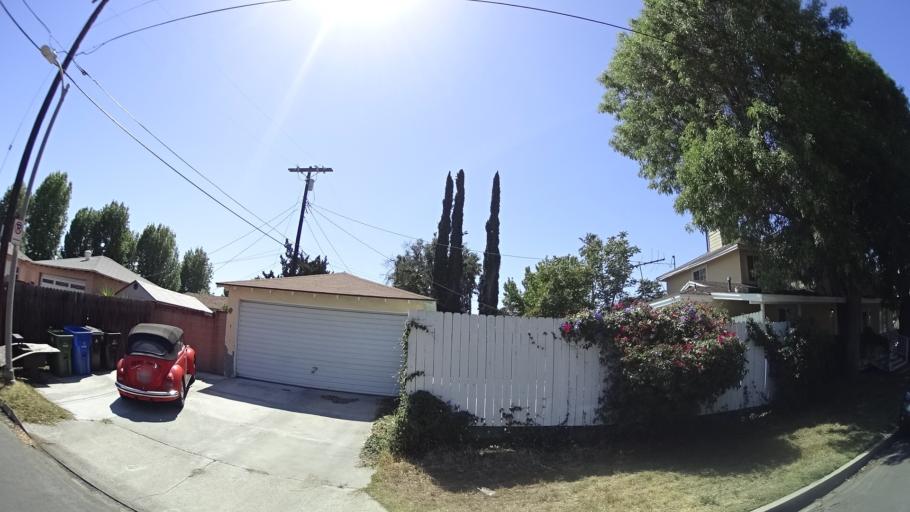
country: US
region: California
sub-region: Los Angeles County
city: North Hollywood
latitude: 34.1781
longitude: -118.4071
